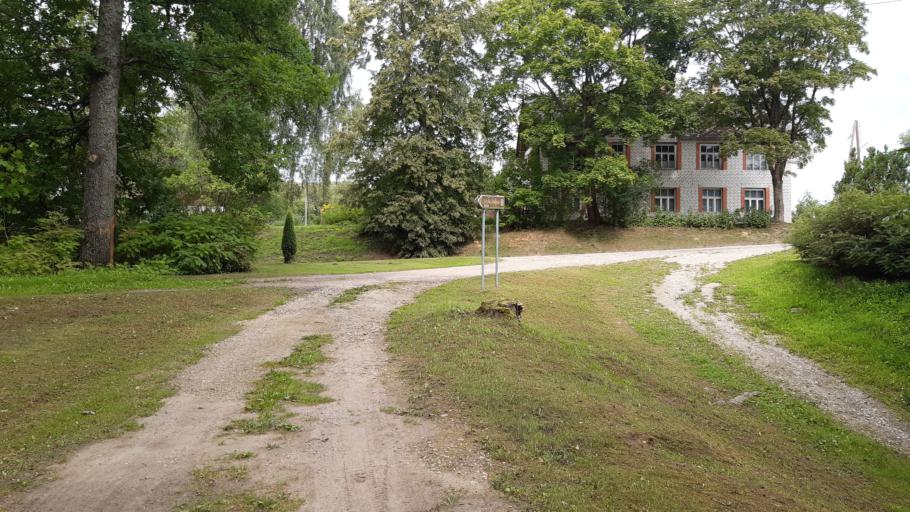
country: LV
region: Strenci
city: Strenci
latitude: 57.5420
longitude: 25.7088
